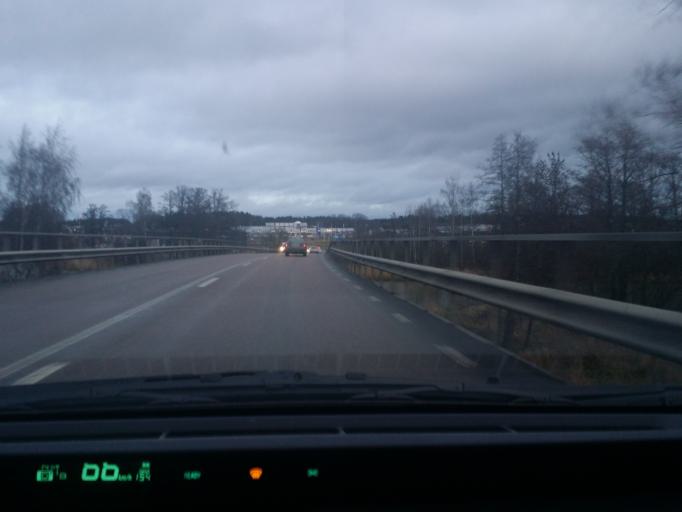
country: SE
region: Soedermanland
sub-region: Eskilstuna Kommun
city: Torshalla
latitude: 59.3844
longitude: 16.4627
